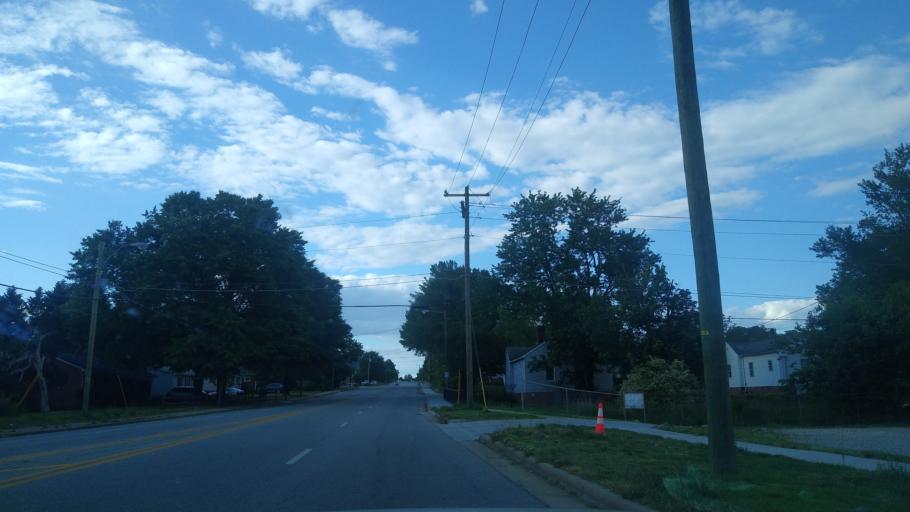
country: US
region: North Carolina
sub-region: Guilford County
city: Greensboro
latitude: 36.1018
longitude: -79.7752
